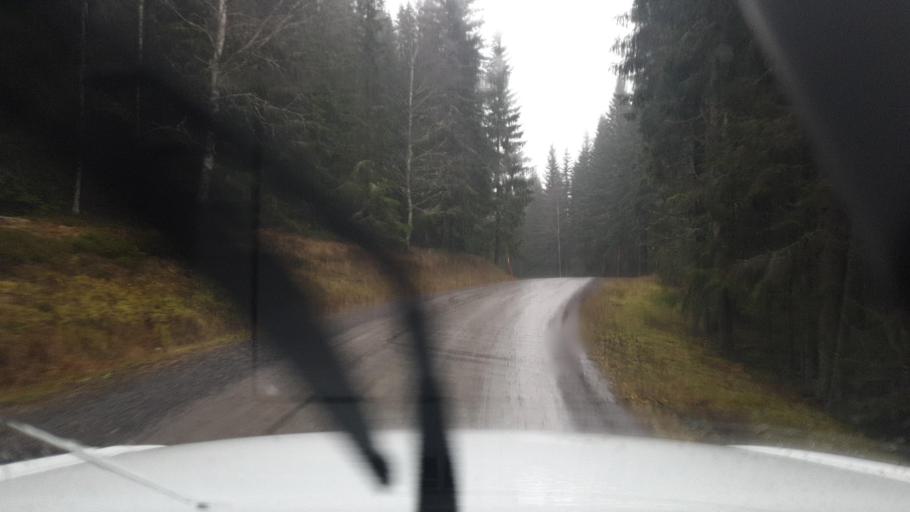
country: SE
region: Vaermland
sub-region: Sunne Kommun
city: Sunne
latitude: 59.8547
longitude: 12.8995
